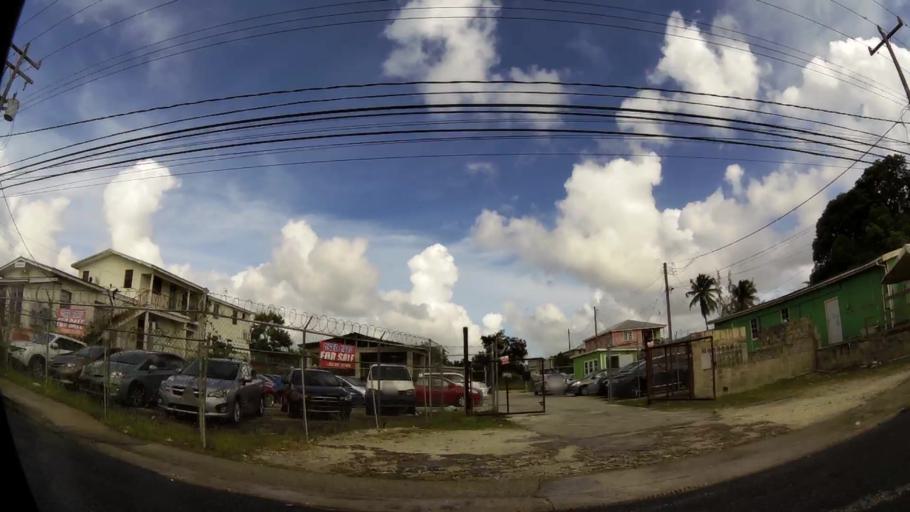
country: BB
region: Saint Michael
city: Bridgetown
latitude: 13.1343
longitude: -59.6057
